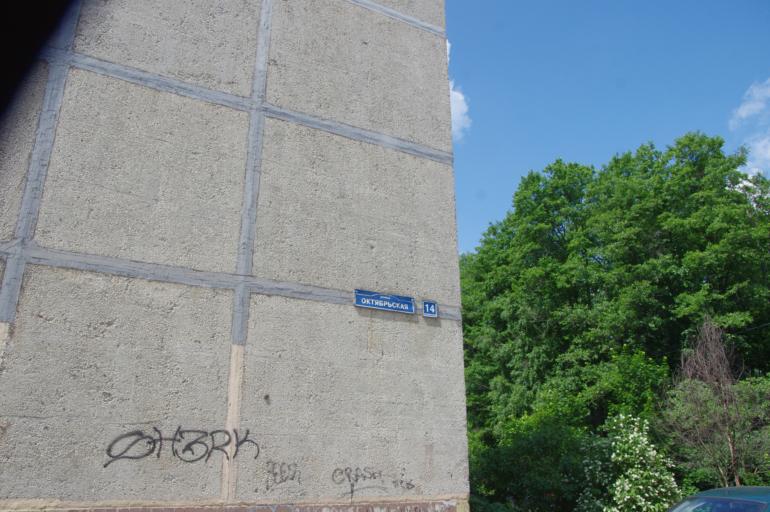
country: RU
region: Moskovskaya
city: Malyshevo
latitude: 55.5452
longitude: 38.3092
